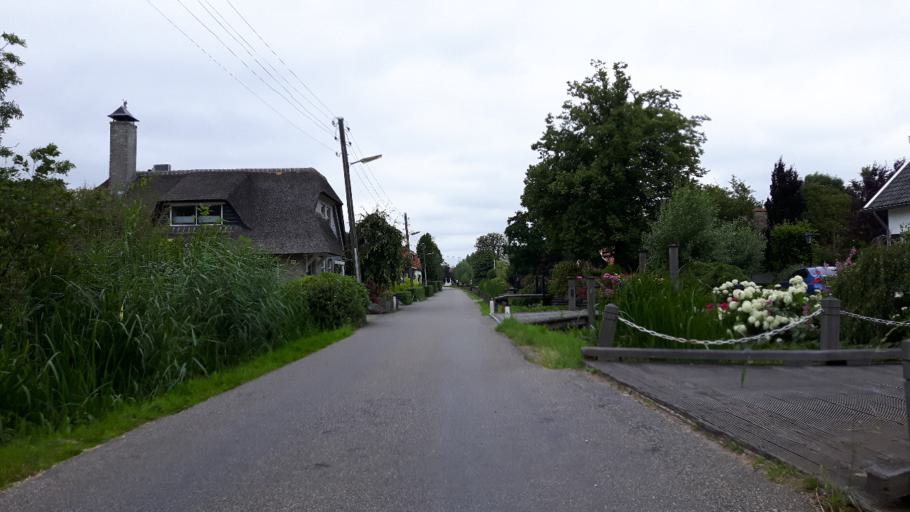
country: NL
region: South Holland
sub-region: Bodegraven-Reeuwijk
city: Reeuwijk
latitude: 52.0413
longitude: 4.7362
